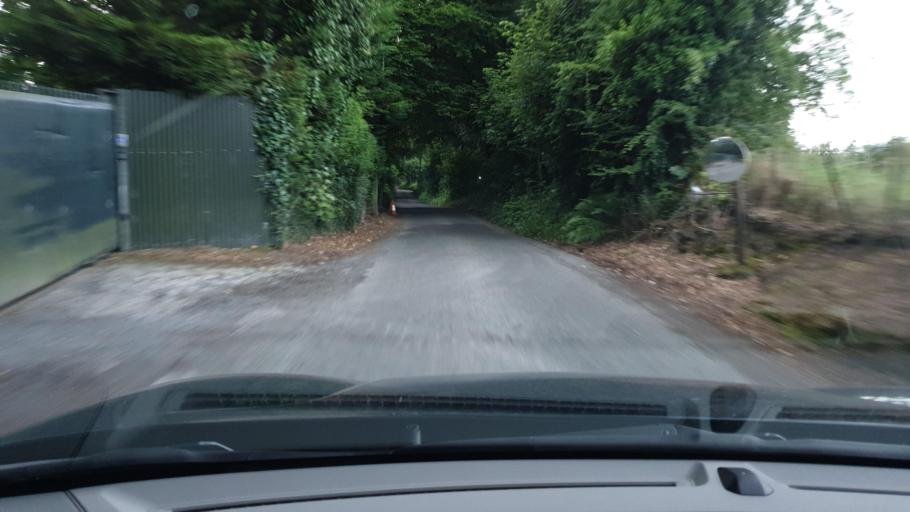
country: IE
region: Leinster
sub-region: Wicklow
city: Blessington
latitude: 53.2267
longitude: -6.5104
